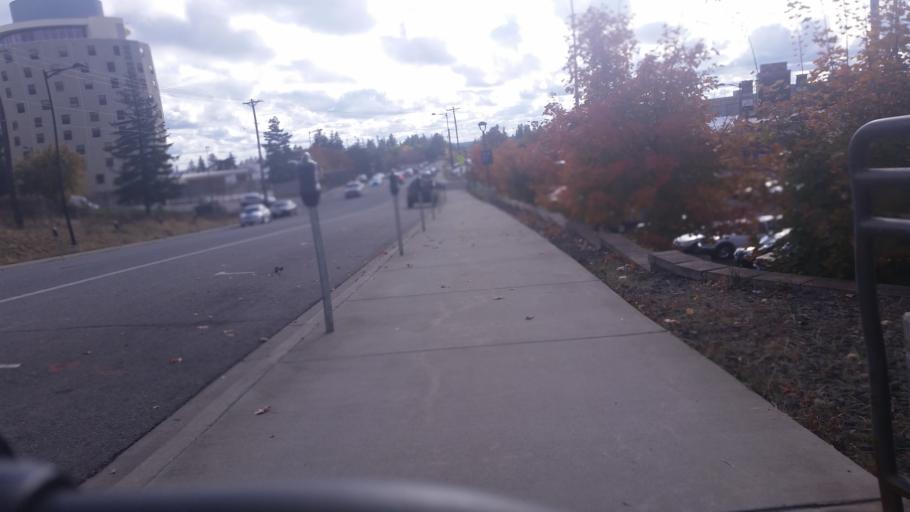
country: US
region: Washington
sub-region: Spokane County
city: Cheney
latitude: 47.4937
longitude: -117.5867
